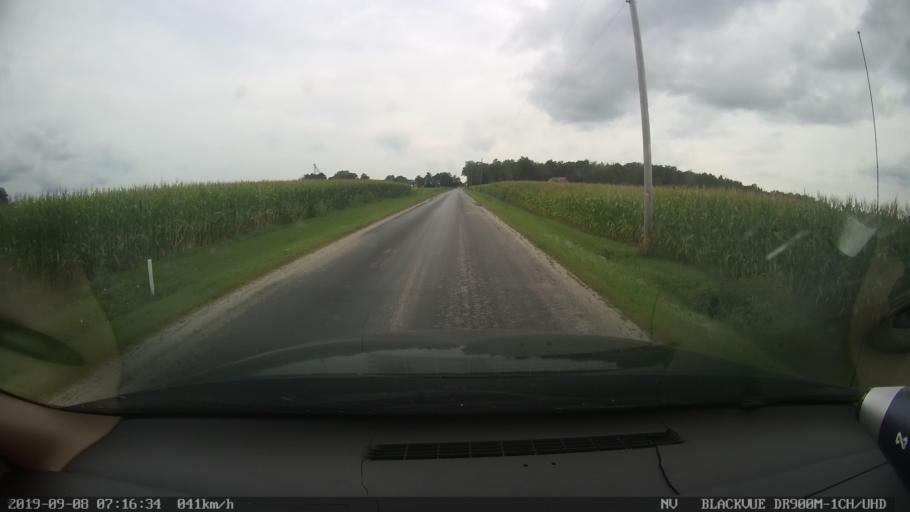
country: US
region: Ohio
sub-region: Richland County
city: Shelby
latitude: 40.9085
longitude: -82.7126
